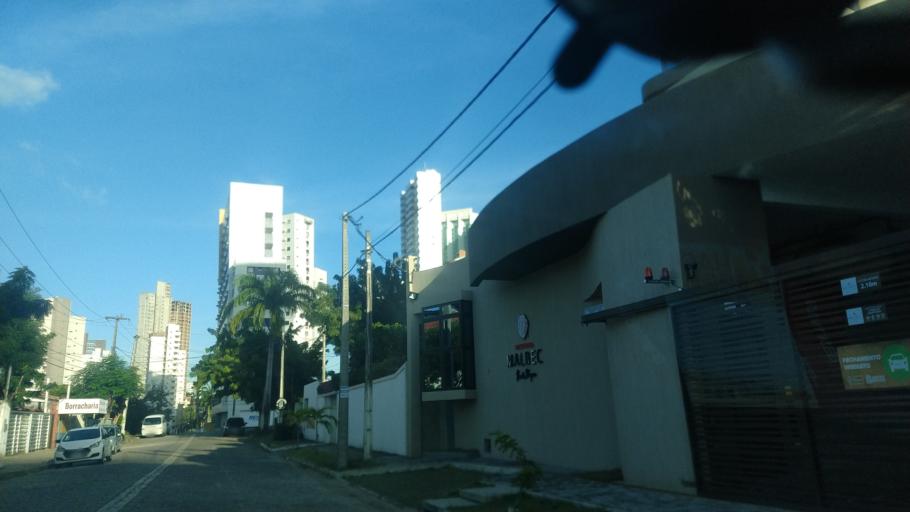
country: BR
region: Rio Grande do Norte
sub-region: Parnamirim
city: Parnamirim
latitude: -5.8824
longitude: -35.1816
